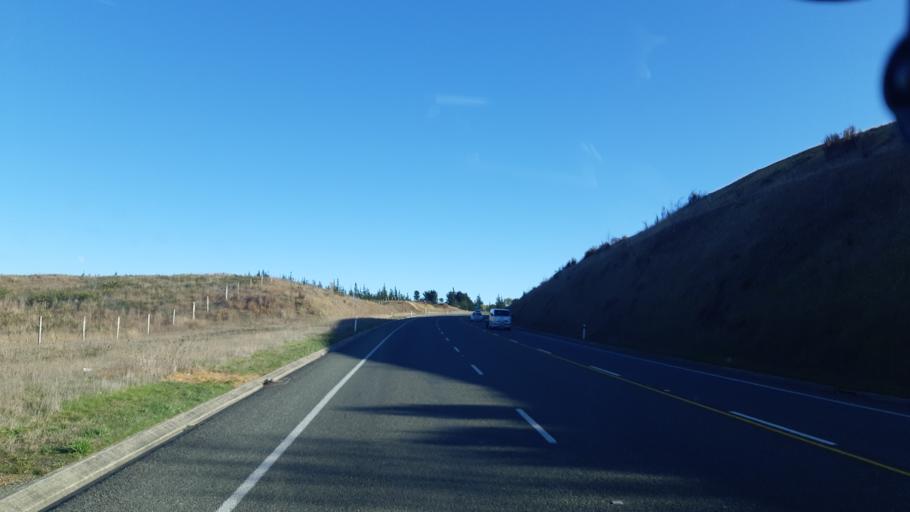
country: NZ
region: Tasman
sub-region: Tasman District
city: Mapua
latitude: -41.2491
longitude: 173.0634
